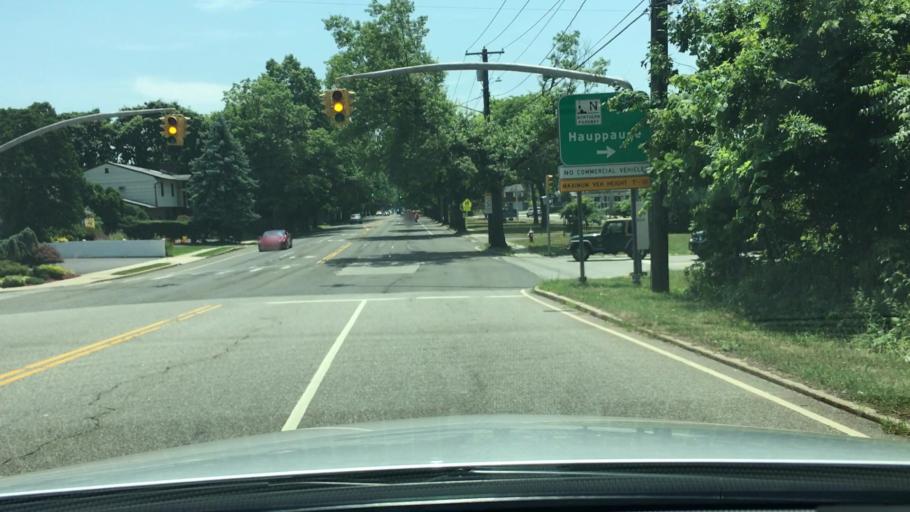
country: US
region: New York
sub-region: Nassau County
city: Plainview
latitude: 40.7949
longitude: -73.4795
